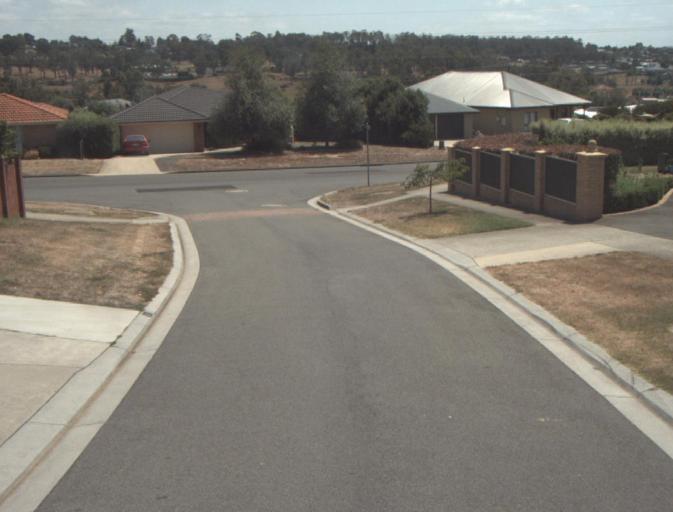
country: AU
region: Tasmania
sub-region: Launceston
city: Newstead
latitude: -41.4797
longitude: 147.1830
